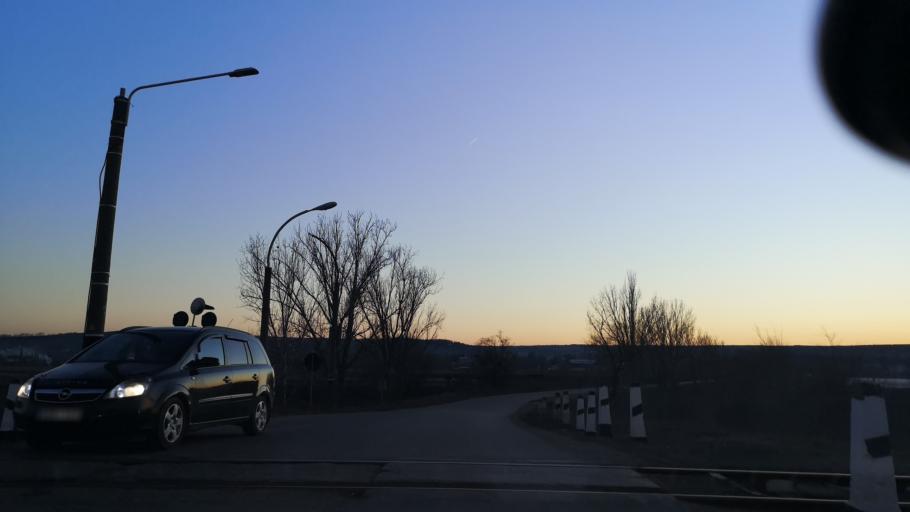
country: MD
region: Anenii Noi
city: Anenii Noi
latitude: 46.8908
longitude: 29.2414
